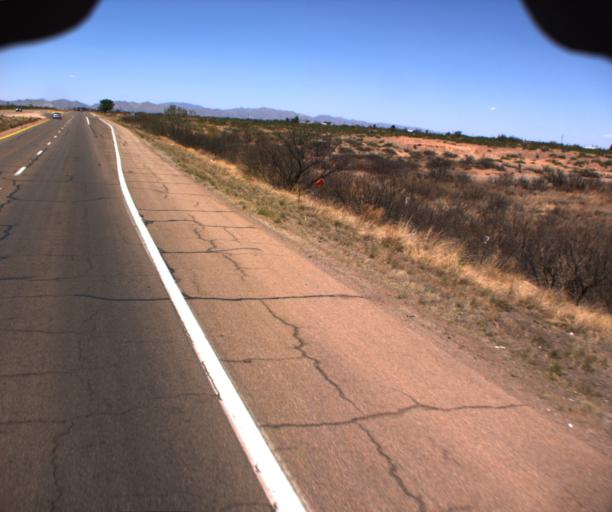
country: US
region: Arizona
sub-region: Cochise County
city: Pirtleville
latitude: 31.3533
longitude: -109.5873
